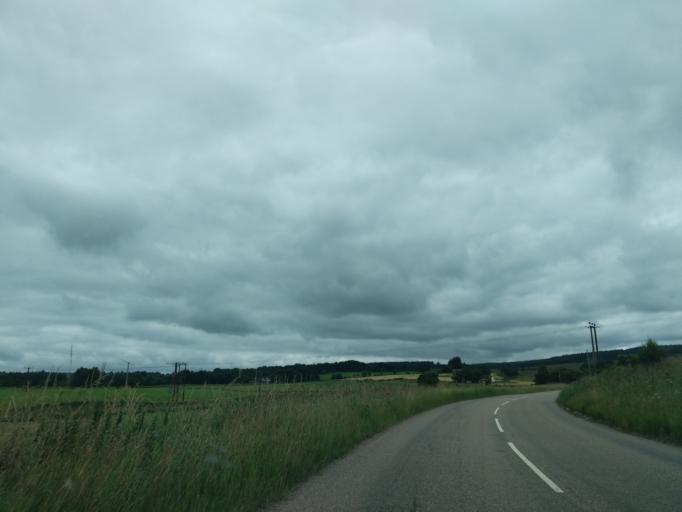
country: GB
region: Scotland
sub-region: Moray
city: Rothes
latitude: 57.4900
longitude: -3.2304
